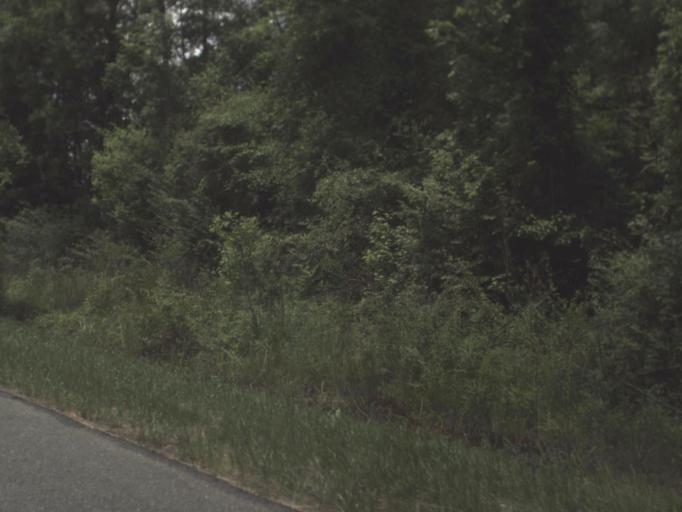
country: US
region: Florida
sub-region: Calhoun County
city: Blountstown
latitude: 30.4176
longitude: -85.0729
